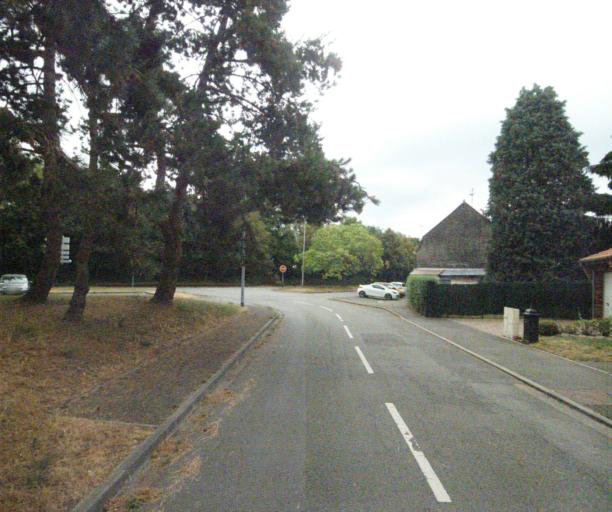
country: FR
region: Nord-Pas-de-Calais
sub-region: Departement du Nord
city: Wasquehal
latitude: 50.6782
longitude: 3.1262
